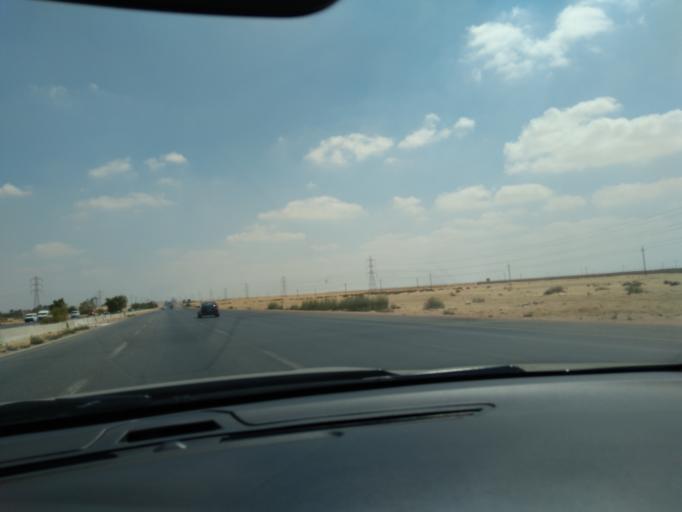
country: EG
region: Al Isma'iliyah
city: At Tall al Kabir
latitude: 30.3617
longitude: 31.9072
